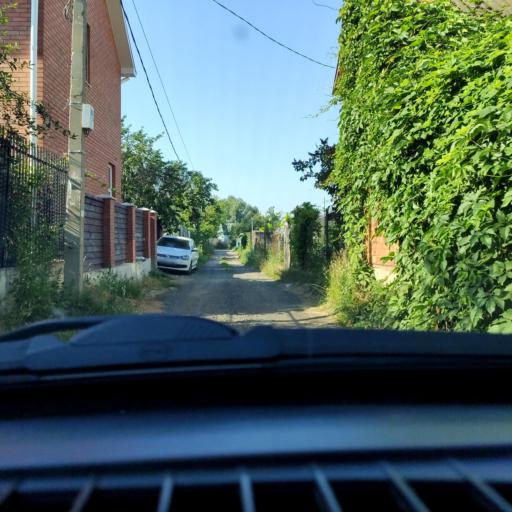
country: RU
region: Samara
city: Zhigulevsk
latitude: 53.4552
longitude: 49.5448
